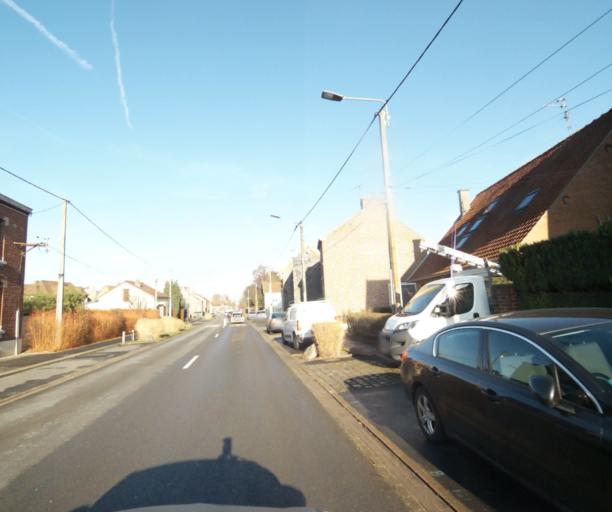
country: FR
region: Nord-Pas-de-Calais
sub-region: Departement du Nord
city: Aulnoy-lez-Valenciennes
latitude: 50.3314
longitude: 3.5233
